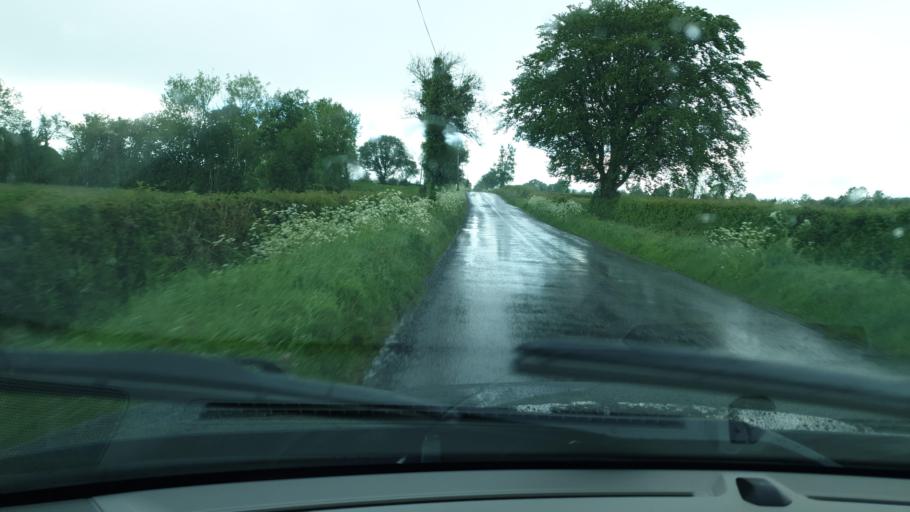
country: IE
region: Leinster
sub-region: Laois
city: Mountmellick
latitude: 53.0937
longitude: -7.3989
